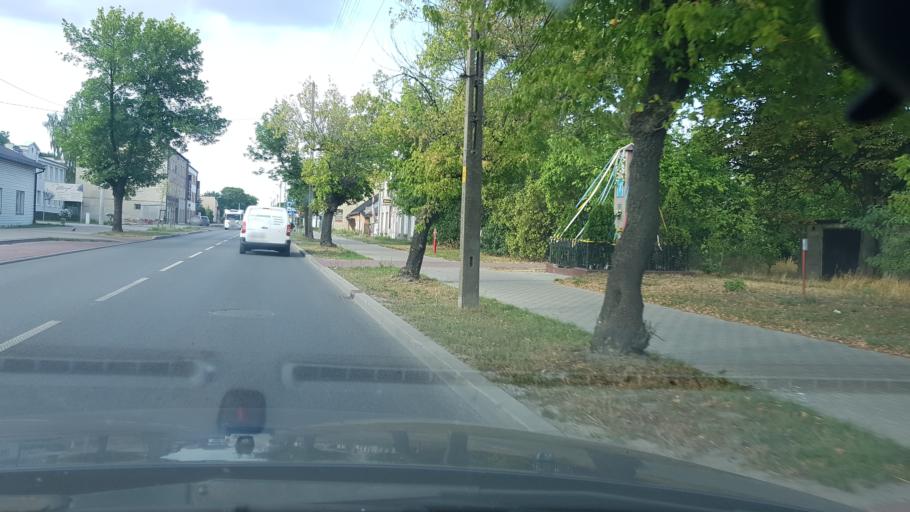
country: PL
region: Lodz Voivodeship
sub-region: Powiat tomaszowski
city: Tomaszow Mazowiecki
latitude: 51.5512
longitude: 20.0167
